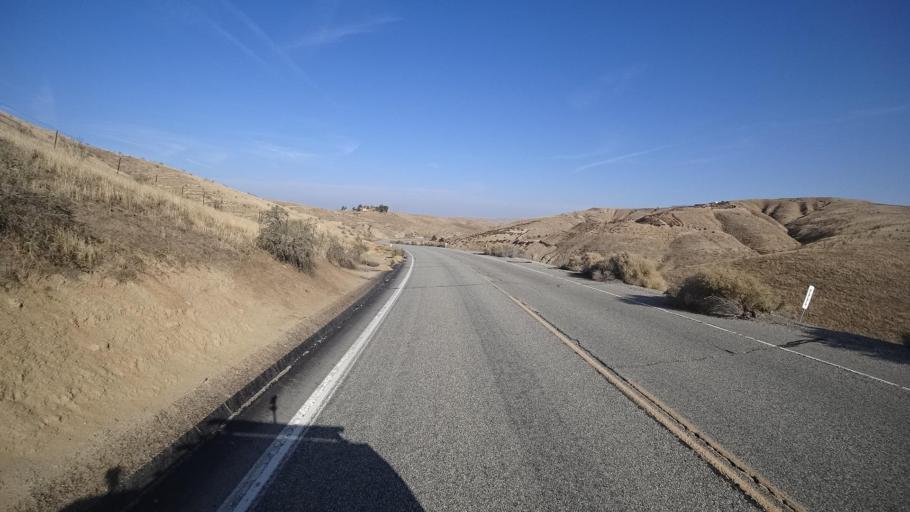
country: US
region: California
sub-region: Kern County
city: Oildale
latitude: 35.5086
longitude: -118.9818
